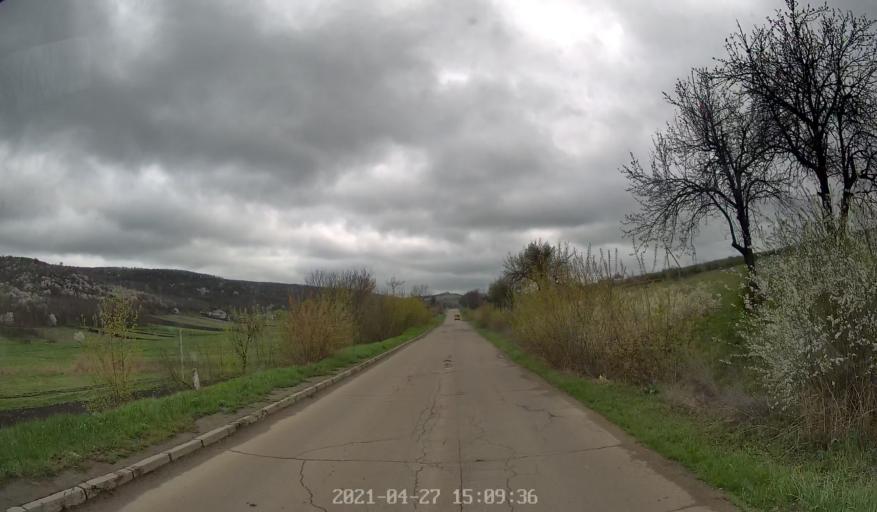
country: MD
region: Chisinau
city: Vadul lui Voda
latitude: 47.0483
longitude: 29.0338
